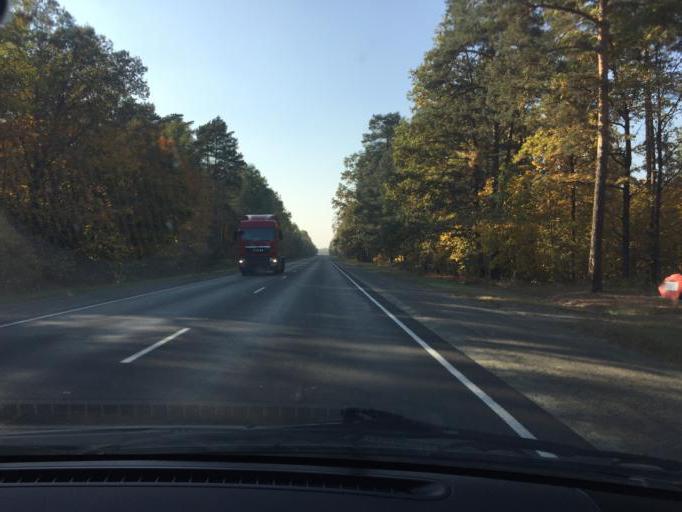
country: BY
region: Brest
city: Mikashevichy
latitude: 52.2455
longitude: 27.4156
